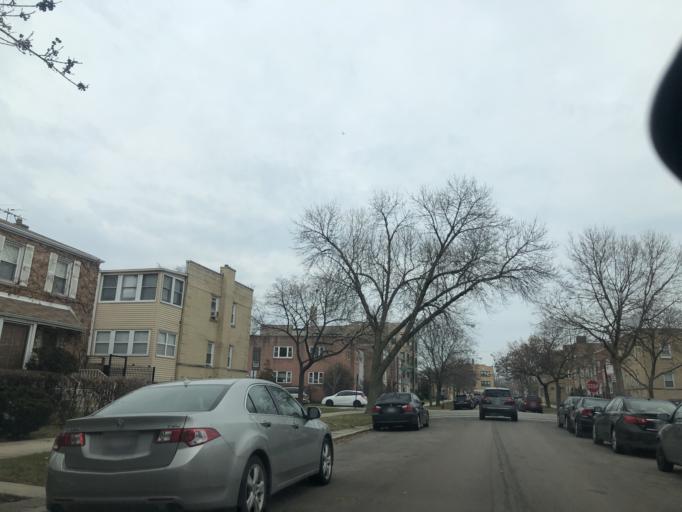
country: US
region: Illinois
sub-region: Cook County
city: Lincolnwood
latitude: 41.9786
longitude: -87.6951
